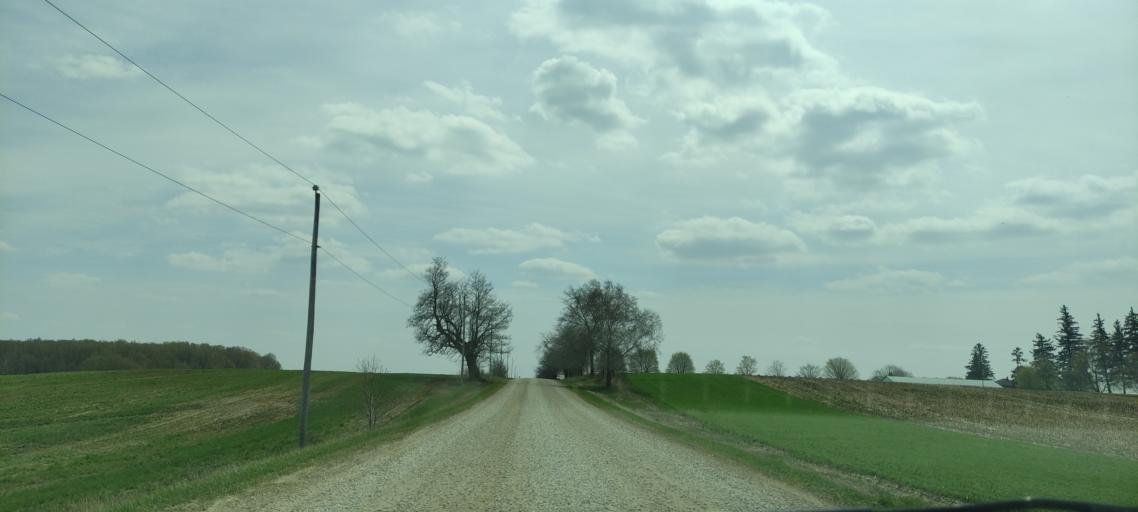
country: CA
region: Ontario
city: Stratford
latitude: 43.3488
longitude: -80.7449
